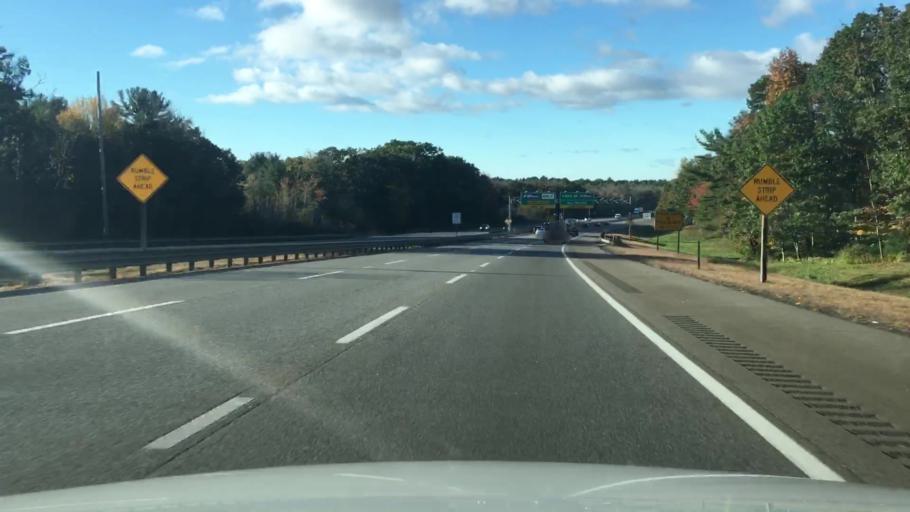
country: US
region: Maine
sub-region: York County
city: York Harbor
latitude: 43.1661
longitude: -70.6541
